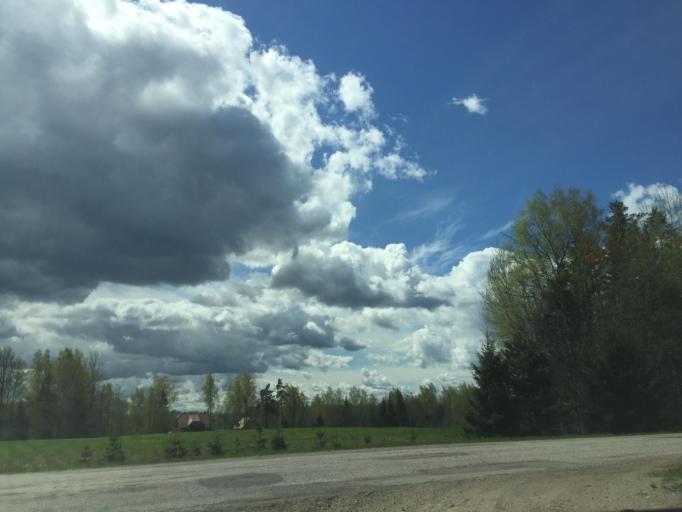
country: LV
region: Vecpiebalga
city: Vecpiebalga
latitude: 56.9970
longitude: 25.9894
